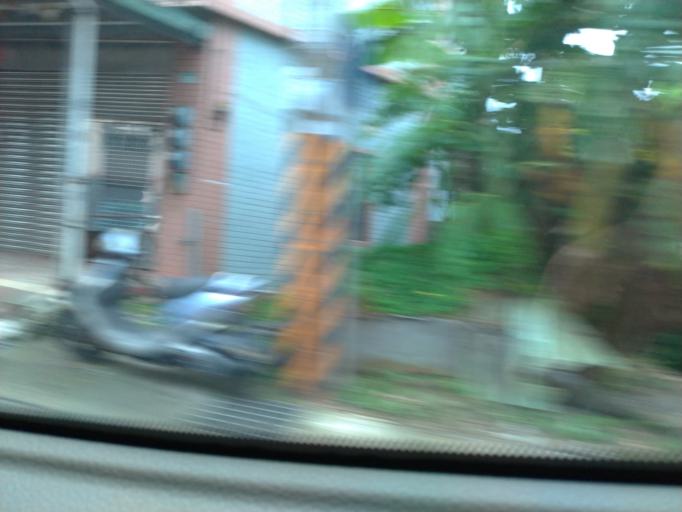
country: TW
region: Taipei
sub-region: Taipei
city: Banqiao
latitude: 24.9335
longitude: 121.4044
